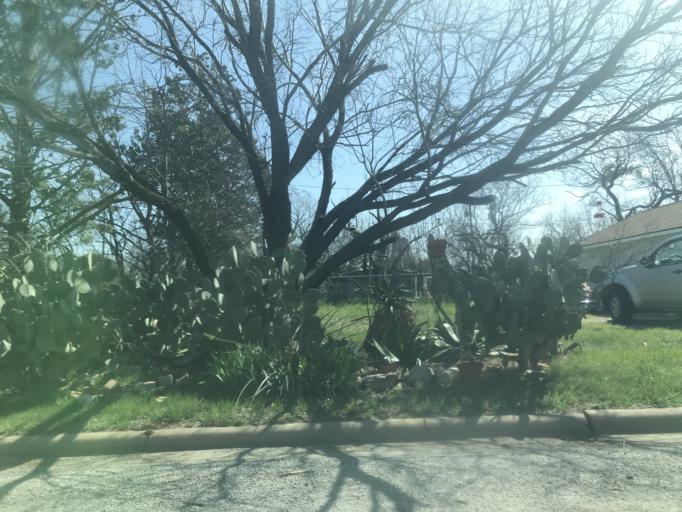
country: US
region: Texas
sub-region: Taylor County
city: Abilene
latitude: 32.4686
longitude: -99.7422
